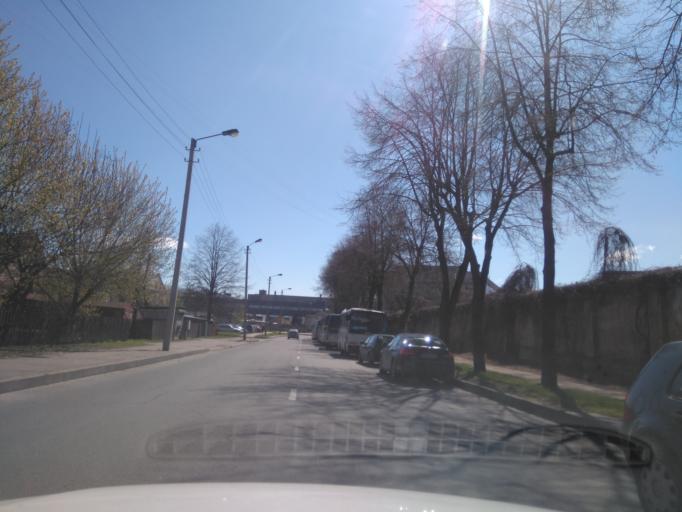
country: LT
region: Kauno apskritis
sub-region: Kaunas
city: Aleksotas
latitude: 54.8885
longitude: 23.9228
